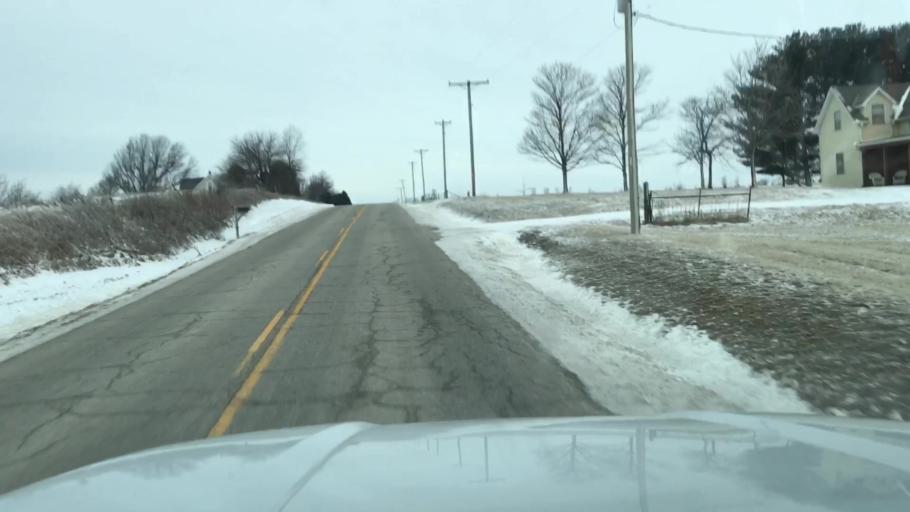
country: US
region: Missouri
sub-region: Andrew County
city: Savannah
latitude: 40.0248
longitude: -94.9292
